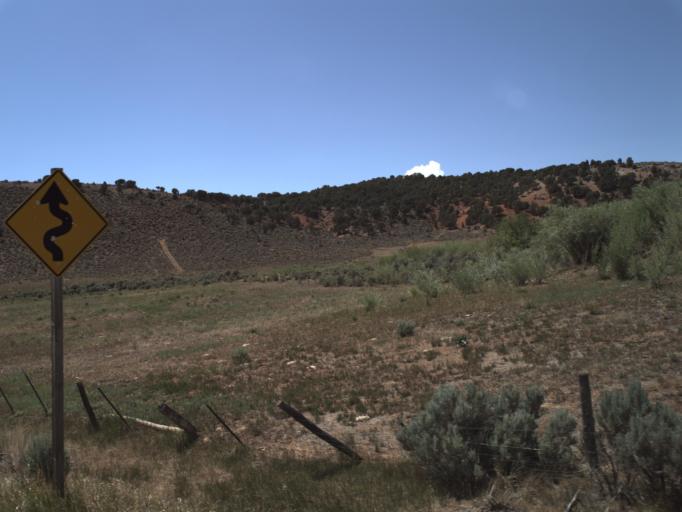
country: US
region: Utah
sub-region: Rich County
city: Randolph
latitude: 41.5040
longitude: -111.2422
